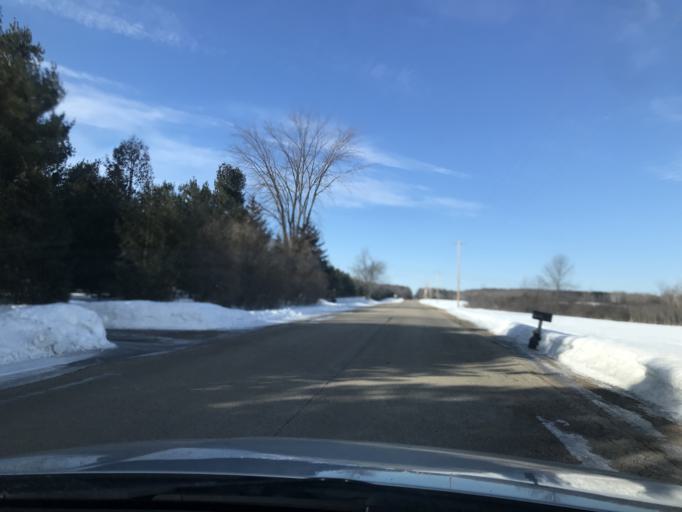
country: US
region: Wisconsin
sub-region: Oconto County
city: Gillett
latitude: 44.9614
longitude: -88.2664
